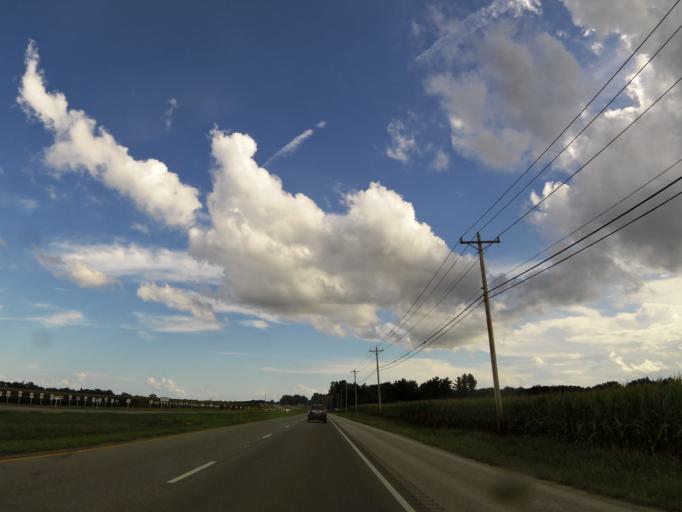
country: US
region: Kentucky
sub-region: Christian County
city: Hopkinsville
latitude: 36.7768
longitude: -87.4731
